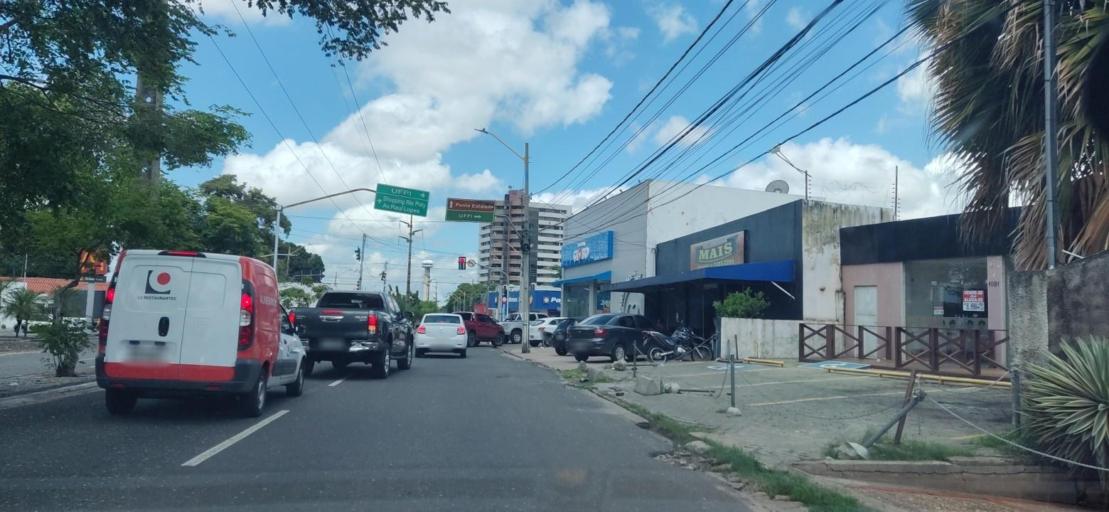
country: BR
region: Piaui
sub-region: Teresina
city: Teresina
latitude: -5.0699
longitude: -42.7918
